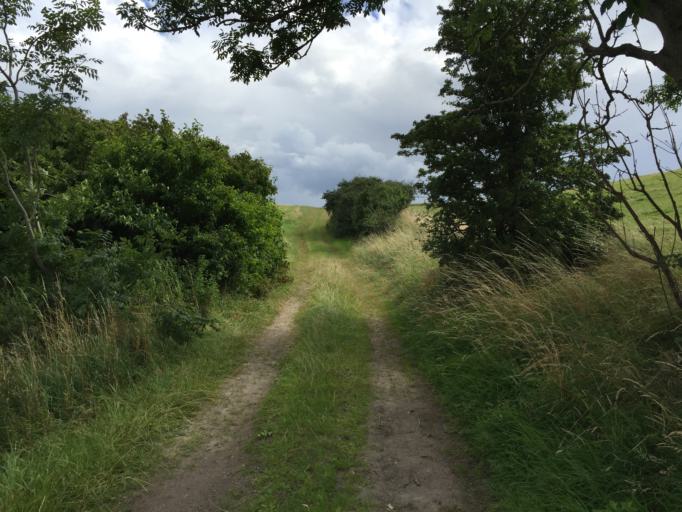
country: DK
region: South Denmark
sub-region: Faaborg-Midtfyn Kommune
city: Faaborg
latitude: 55.0596
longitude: 10.2551
